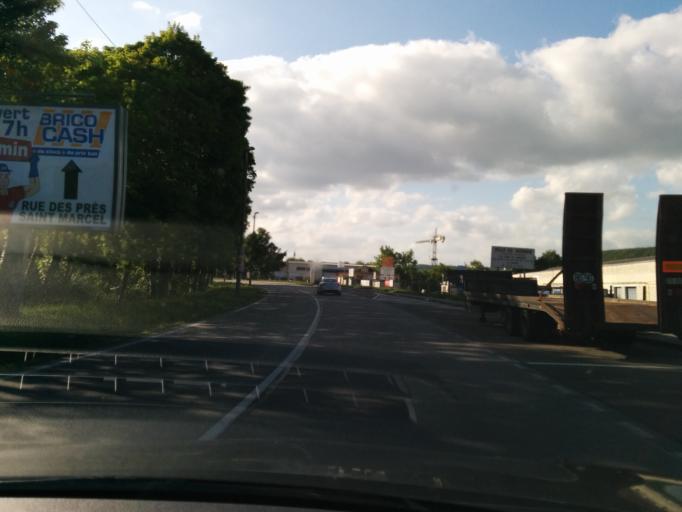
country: FR
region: Haute-Normandie
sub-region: Departement de l'Eure
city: Vernon
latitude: 49.0818
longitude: 1.5041
